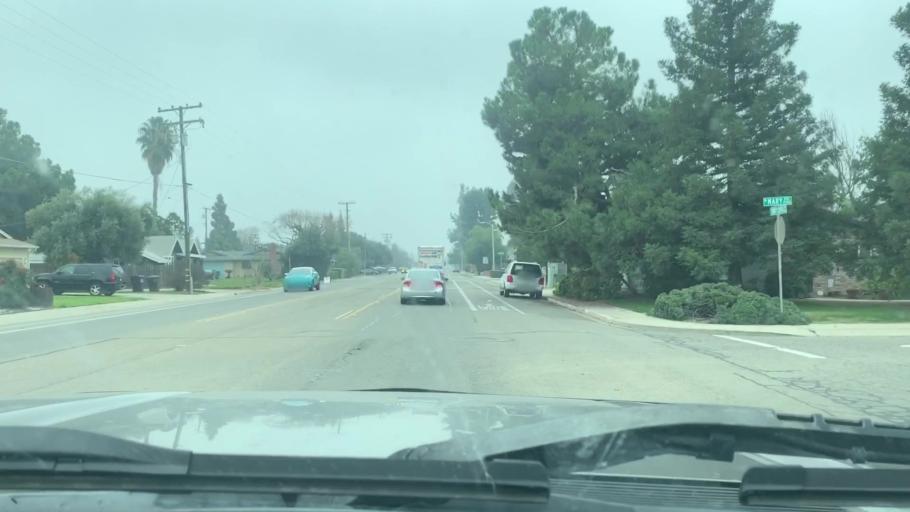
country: US
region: California
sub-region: Tulare County
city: Visalia
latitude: 36.3101
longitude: -119.3228
